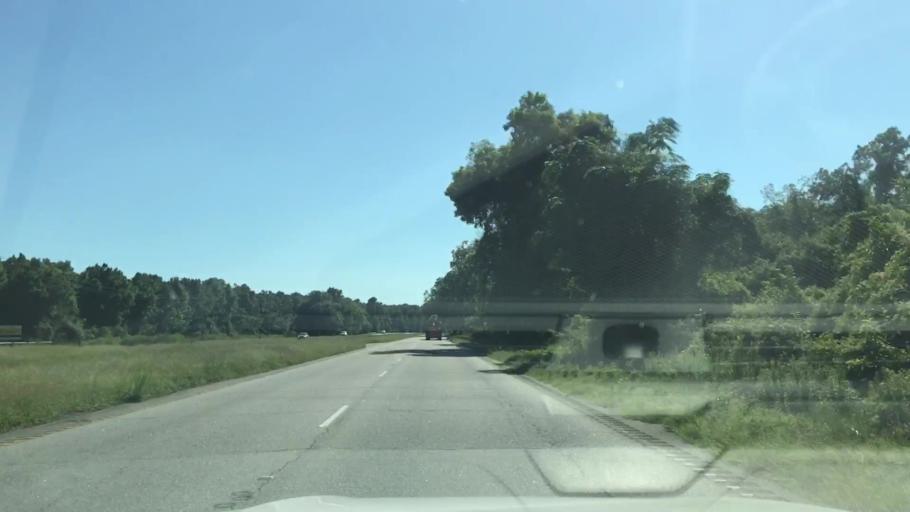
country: US
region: South Carolina
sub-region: Charleston County
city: Awendaw
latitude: 33.0579
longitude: -79.5429
